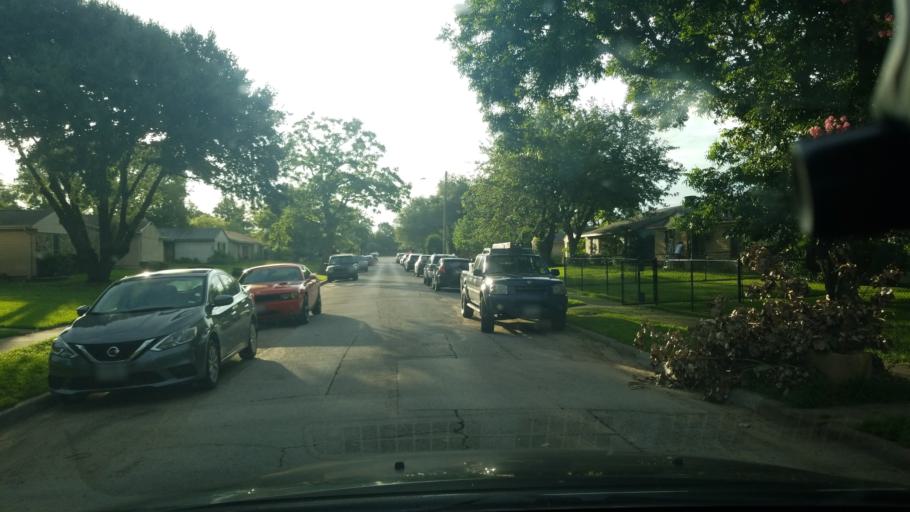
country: US
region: Texas
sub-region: Dallas County
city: Balch Springs
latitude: 32.7437
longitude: -96.6505
